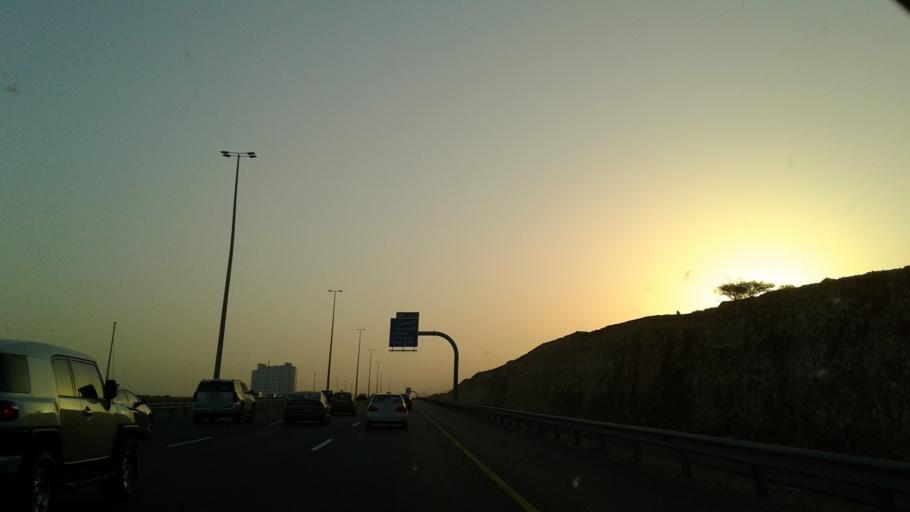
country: OM
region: Muhafazat Masqat
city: Bawshar
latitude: 23.5660
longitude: 58.3649
